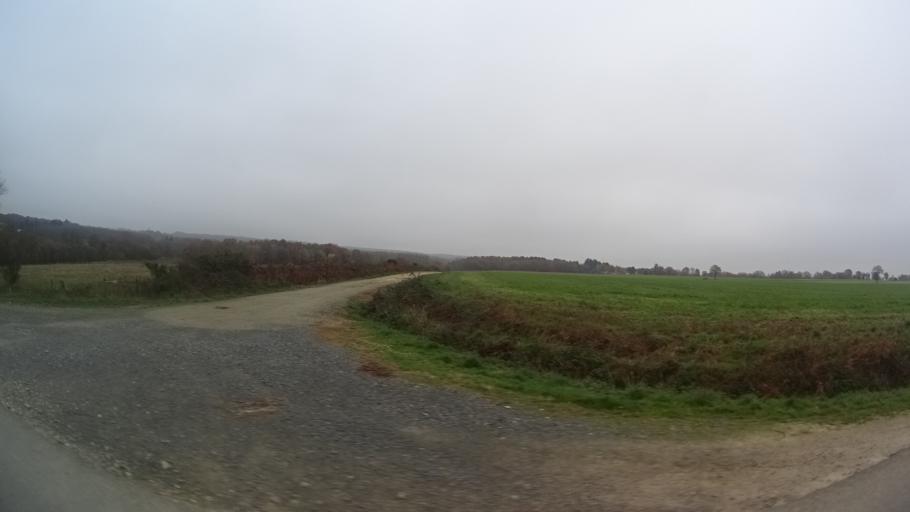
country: FR
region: Brittany
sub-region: Departement d'Ille-et-Vilaine
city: Sainte-Marie
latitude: 47.7071
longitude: -1.9935
